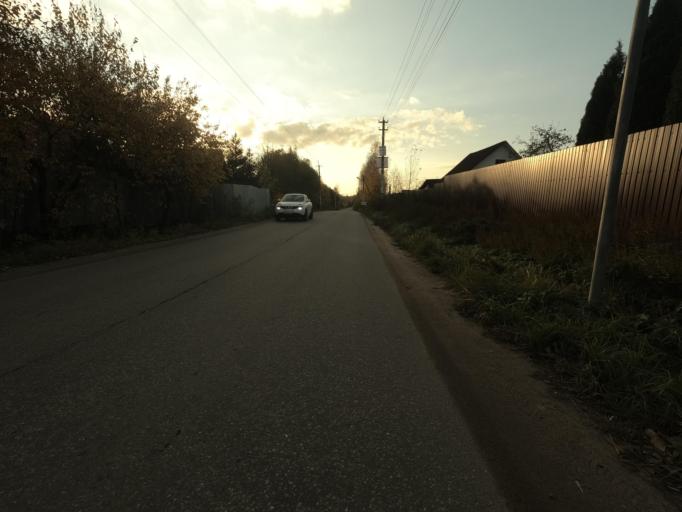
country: RU
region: St.-Petersburg
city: Beloostrov
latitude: 60.1881
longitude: 30.0760
